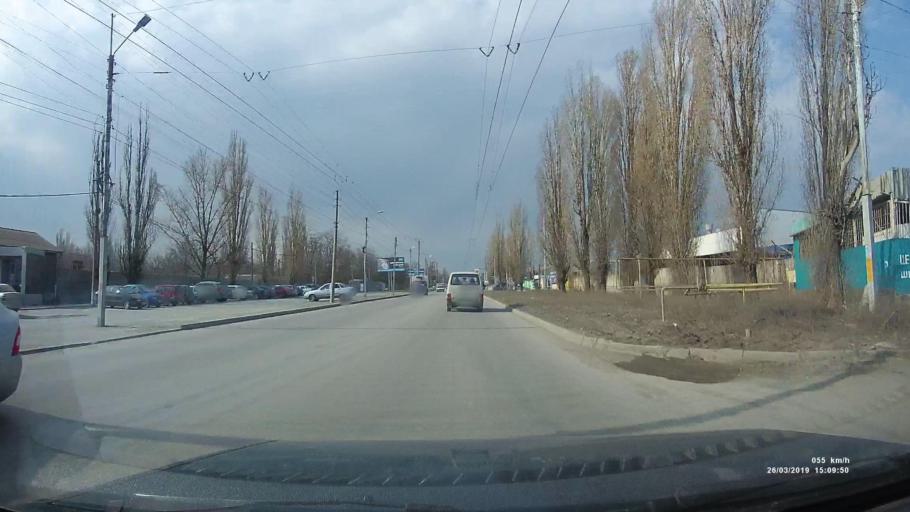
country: RU
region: Rostov
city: Taganrog
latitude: 47.2500
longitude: 38.8771
